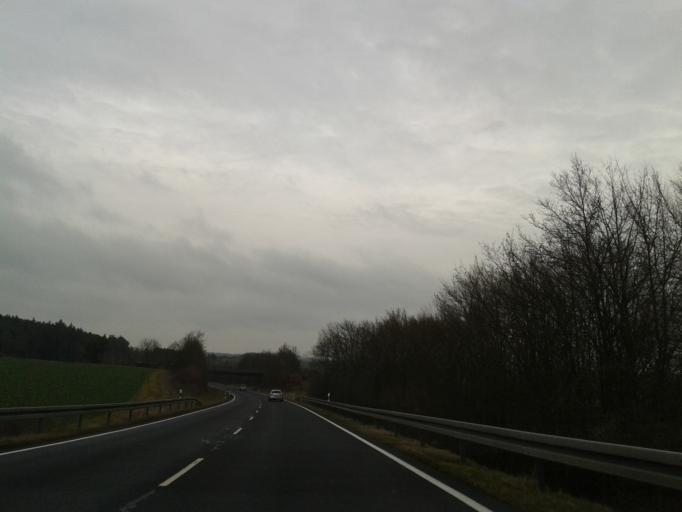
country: DE
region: Bavaria
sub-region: Regierungsbezirk Unterfranken
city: Burgpreppach
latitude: 50.1346
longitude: 10.6294
